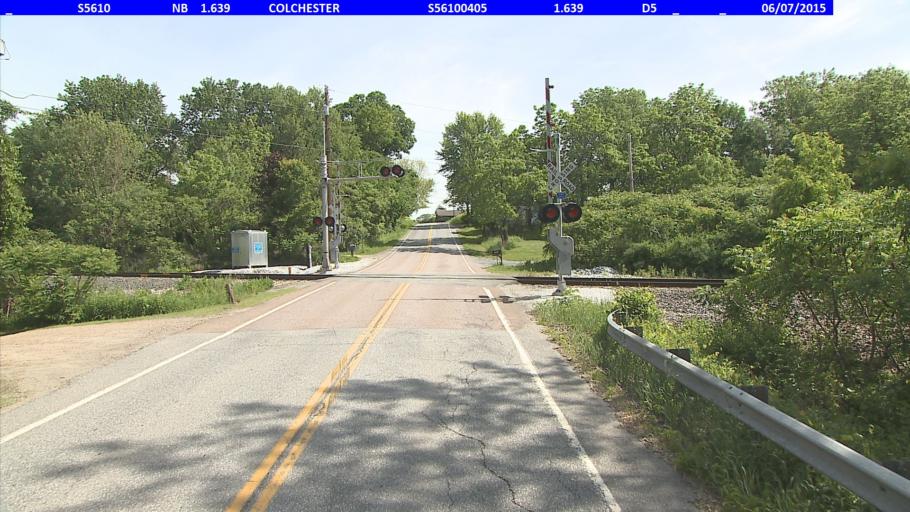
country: US
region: Vermont
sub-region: Chittenden County
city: Colchester
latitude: 44.5636
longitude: -73.1311
